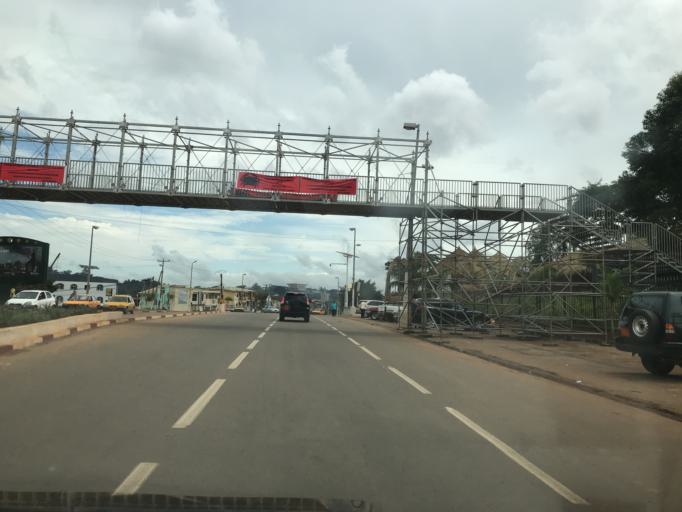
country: CM
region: Centre
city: Yaounde
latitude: 3.8943
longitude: 11.5004
